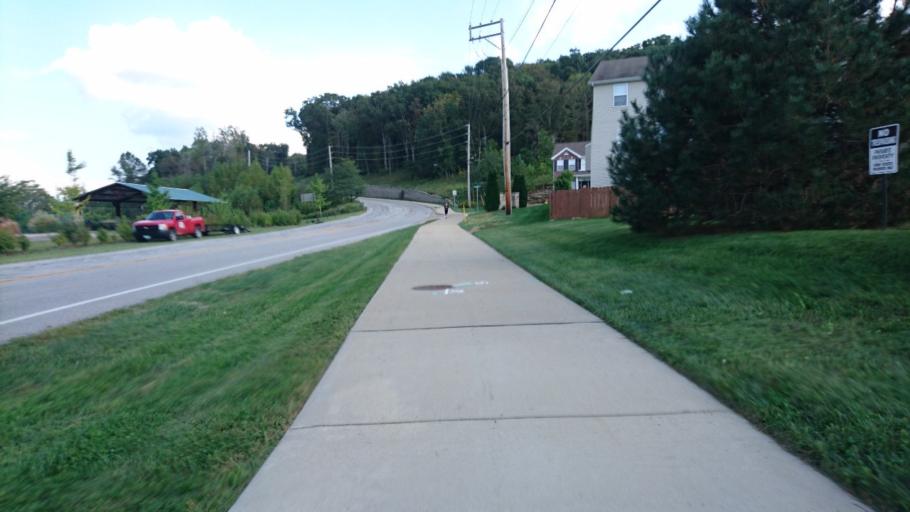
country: US
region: Missouri
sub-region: Saint Louis County
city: Eureka
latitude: 38.5156
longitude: -90.6365
